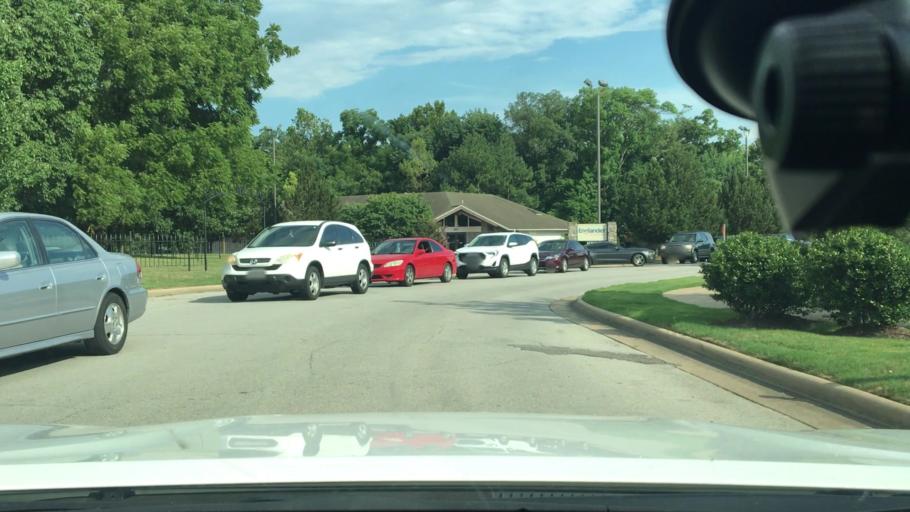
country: US
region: Arkansas
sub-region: Benton County
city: Bentonville
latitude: 36.3342
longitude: -94.1874
